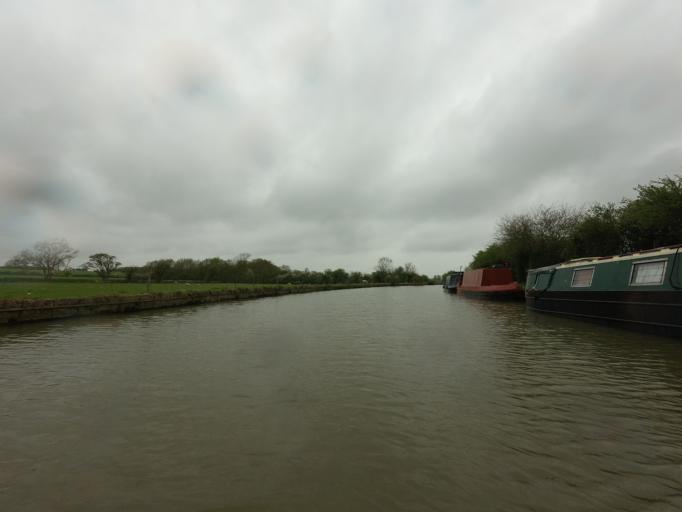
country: GB
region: England
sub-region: Northamptonshire
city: Roade
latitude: 52.1199
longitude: -0.8903
